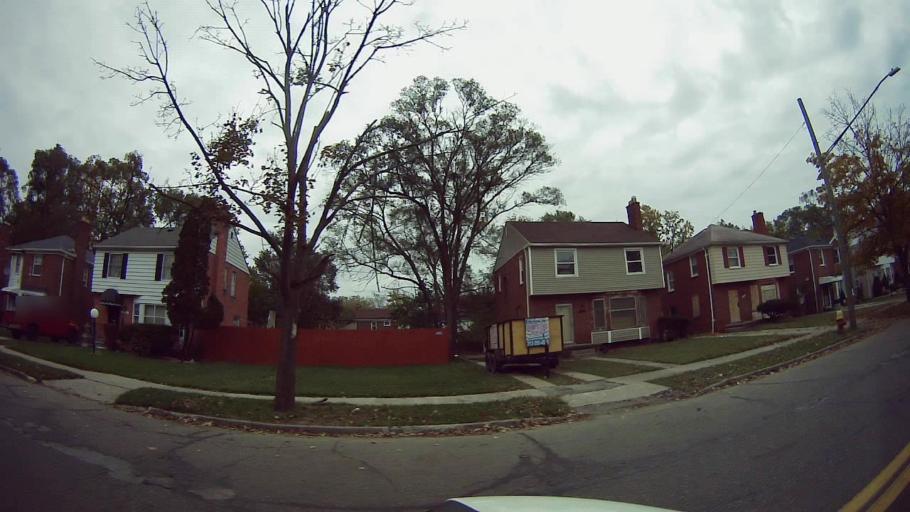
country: US
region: Michigan
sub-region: Oakland County
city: Oak Park
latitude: 42.4132
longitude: -83.1895
